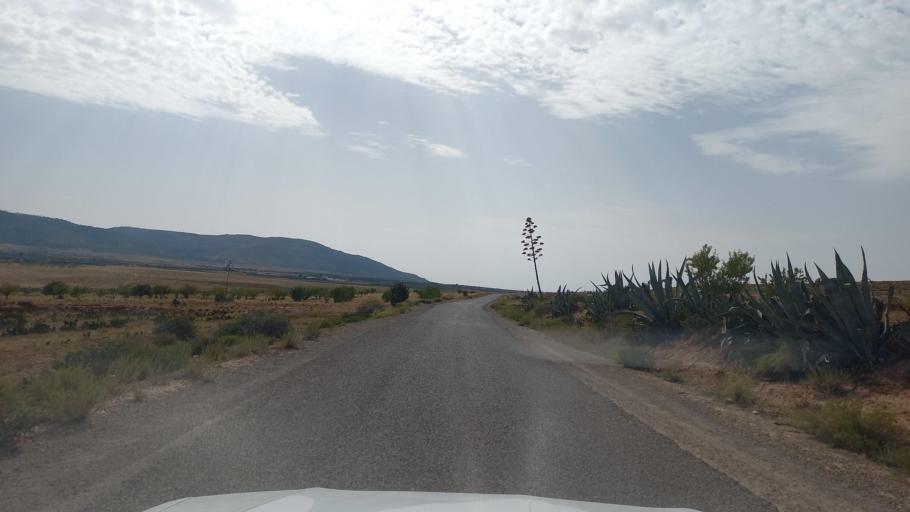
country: TN
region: Al Qasrayn
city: Kasserine
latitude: 35.3607
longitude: 8.8436
